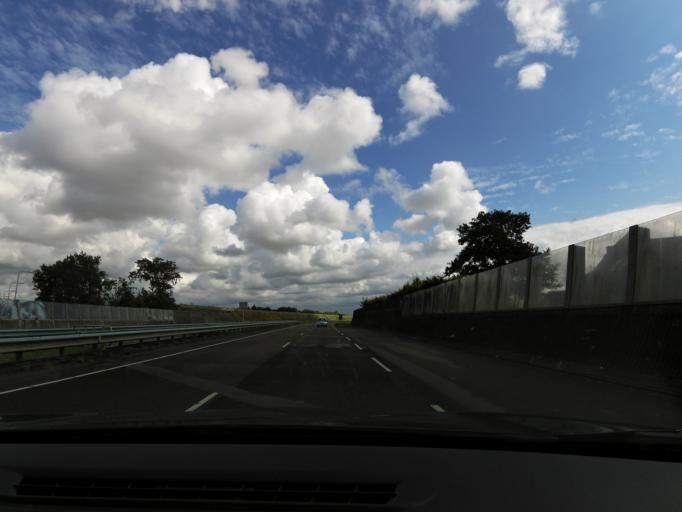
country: NL
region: South Holland
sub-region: Gemeente Westland
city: Kwintsheul
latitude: 52.0280
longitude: 4.2605
